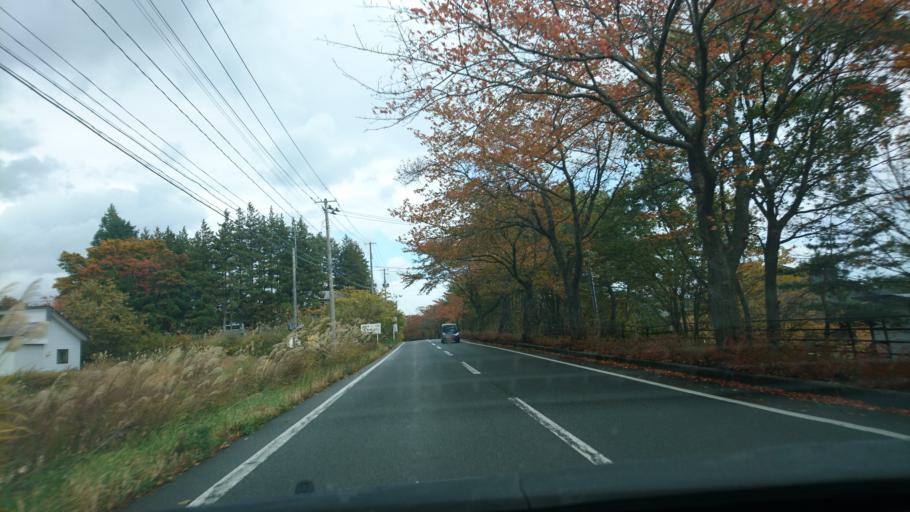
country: JP
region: Iwate
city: Shizukuishi
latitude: 39.6924
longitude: 141.0233
